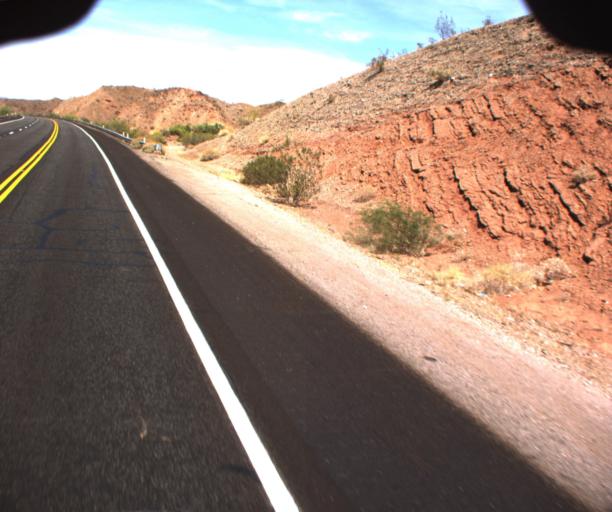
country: US
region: Arizona
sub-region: La Paz County
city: Cienega Springs
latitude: 34.2268
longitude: -114.1828
